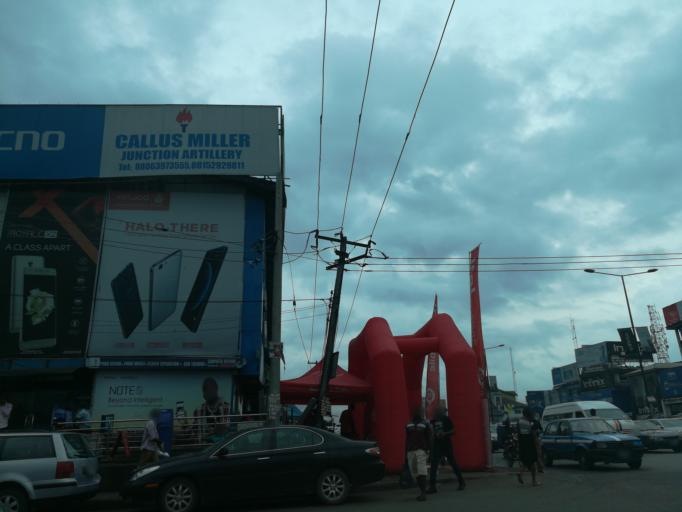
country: NG
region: Rivers
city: Port Harcourt
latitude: 4.8434
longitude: 7.0383
